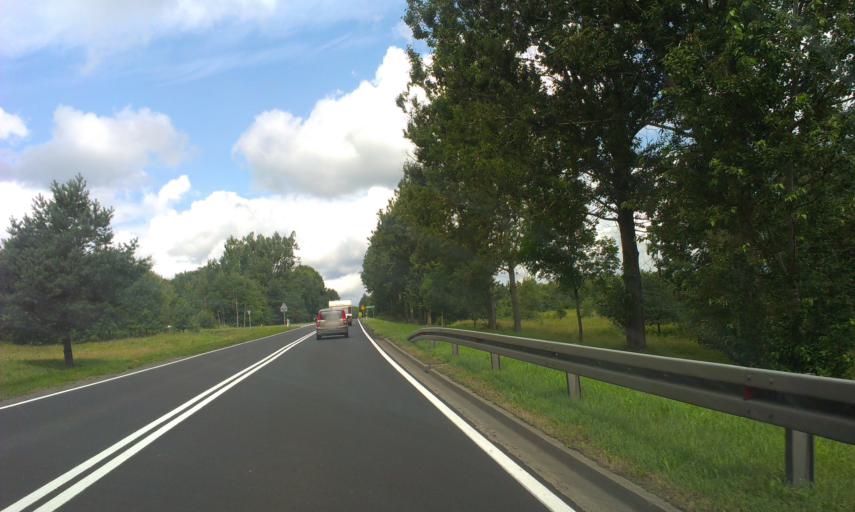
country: PL
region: West Pomeranian Voivodeship
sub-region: Powiat koszalinski
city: Bobolice
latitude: 53.9874
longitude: 16.5381
